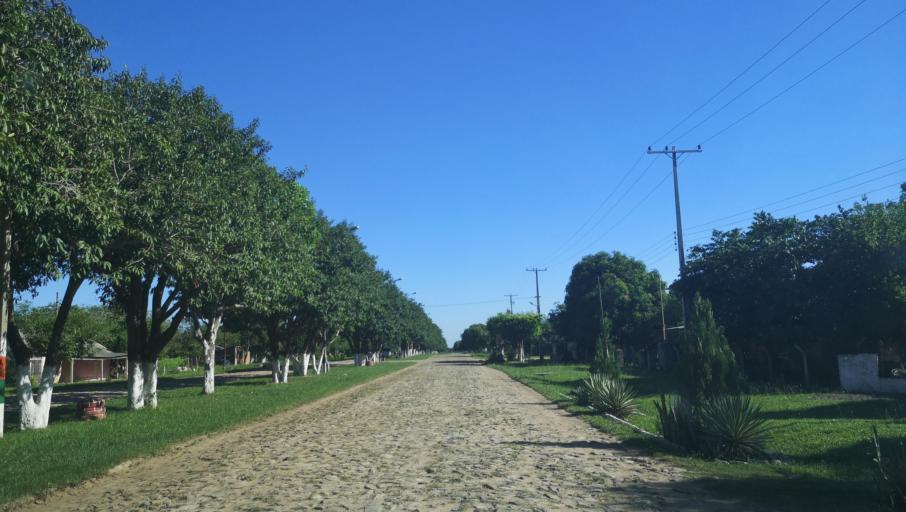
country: PY
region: Caaguazu
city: Carayao
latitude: -25.1985
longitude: -56.4004
